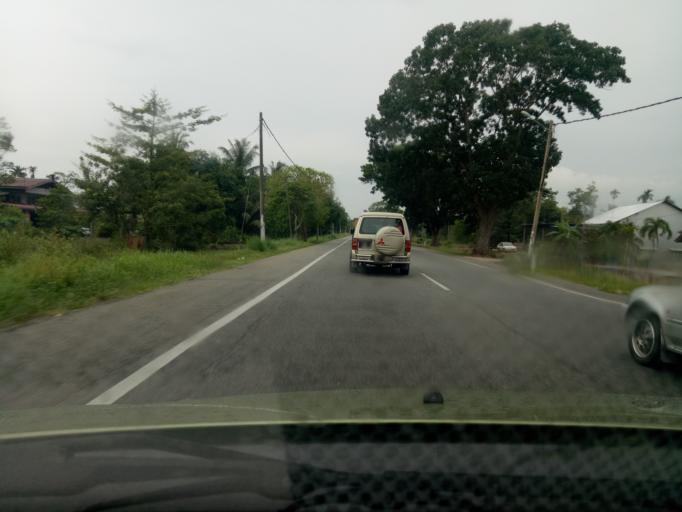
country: MY
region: Kedah
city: Gurun
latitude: 5.8926
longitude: 100.4402
